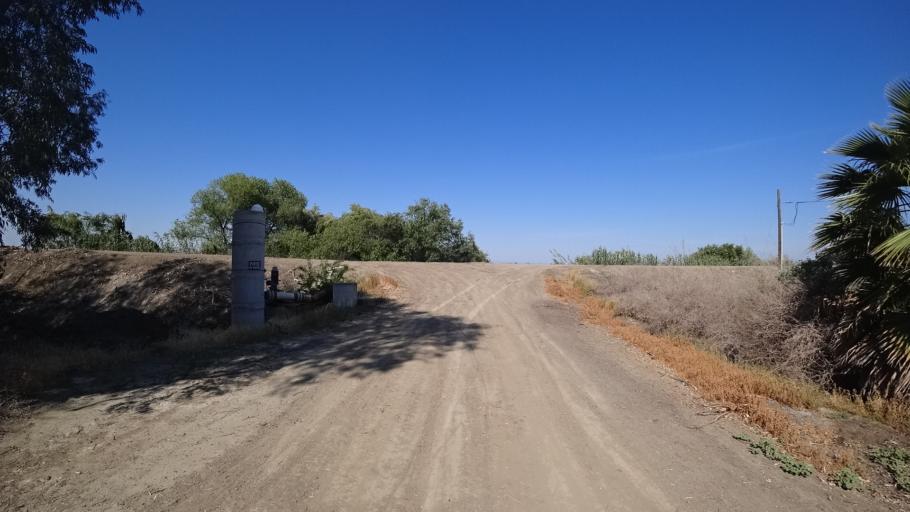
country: US
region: California
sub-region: Fresno County
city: Riverdale
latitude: 36.3511
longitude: -119.8969
